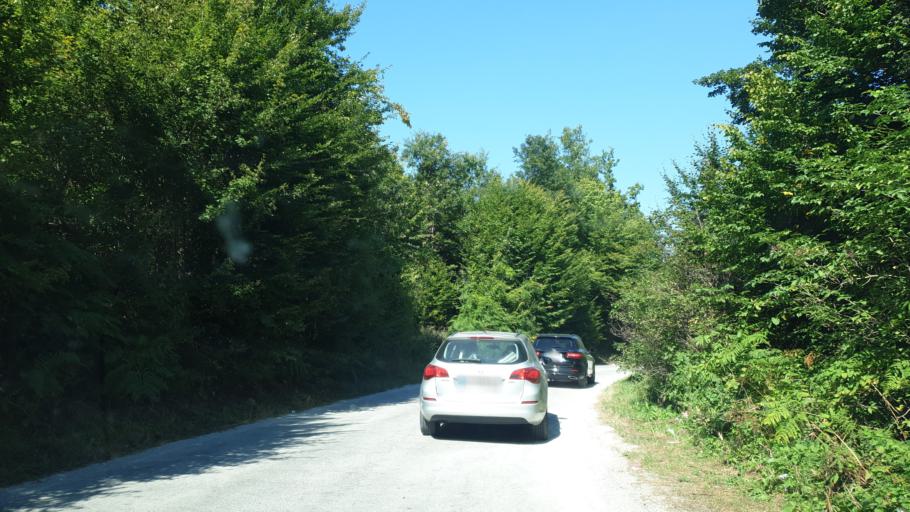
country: RS
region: Central Serbia
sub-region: Zlatiborski Okrug
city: Cajetina
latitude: 43.7029
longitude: 19.8449
